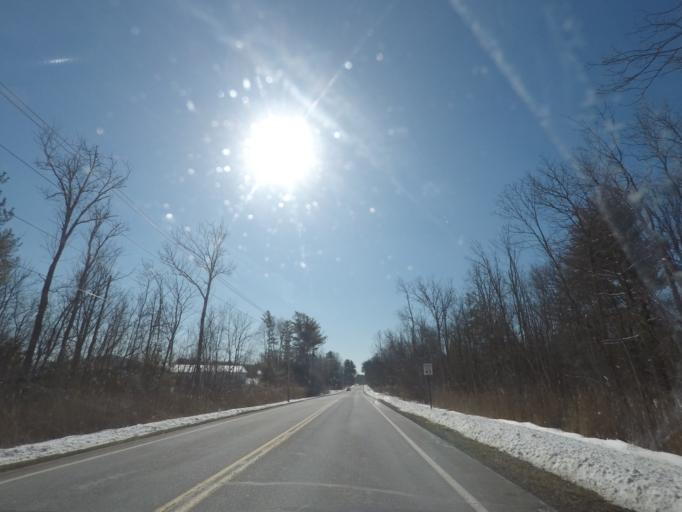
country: US
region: New York
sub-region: Saratoga County
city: Country Knolls
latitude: 42.9332
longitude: -73.8248
